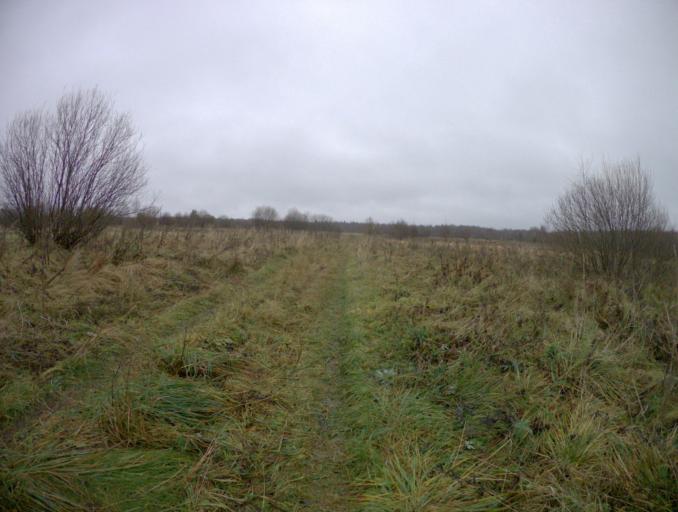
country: RU
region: Vladimir
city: Golovino
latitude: 55.9781
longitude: 40.4932
